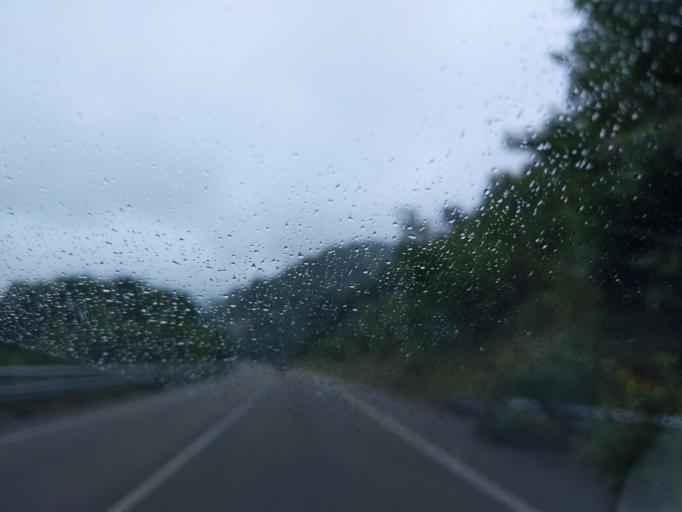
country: ES
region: Asturias
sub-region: Province of Asturias
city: El entrego
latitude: 43.2965
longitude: -5.6100
